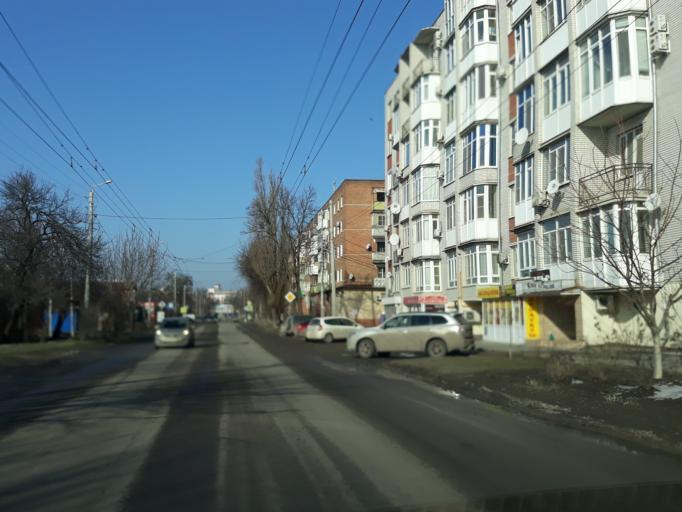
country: RU
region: Rostov
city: Taganrog
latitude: 47.2032
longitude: 38.9014
